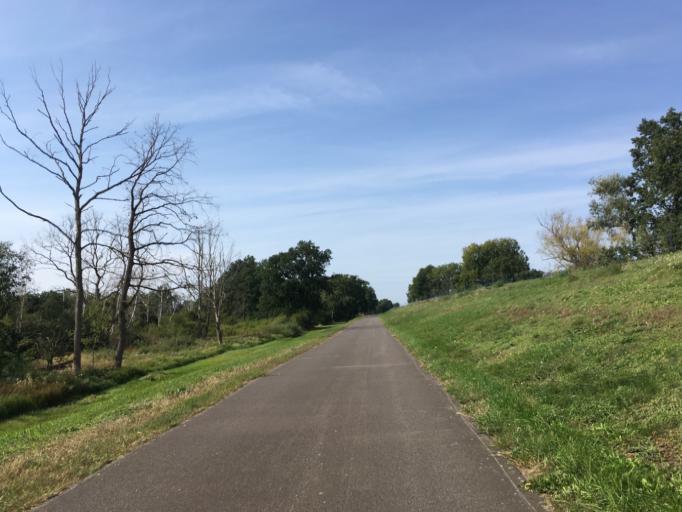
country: DE
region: Brandenburg
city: Vogelsang
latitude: 52.1782
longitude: 14.6959
